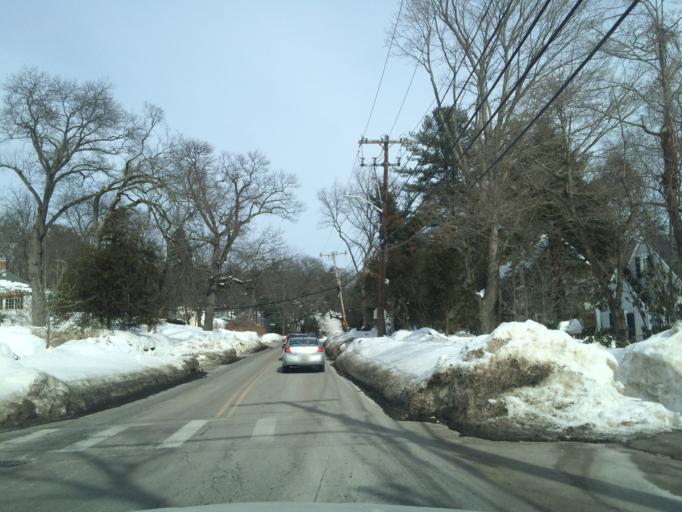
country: US
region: Massachusetts
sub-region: Middlesex County
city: Newton
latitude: 42.3053
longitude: -71.1750
